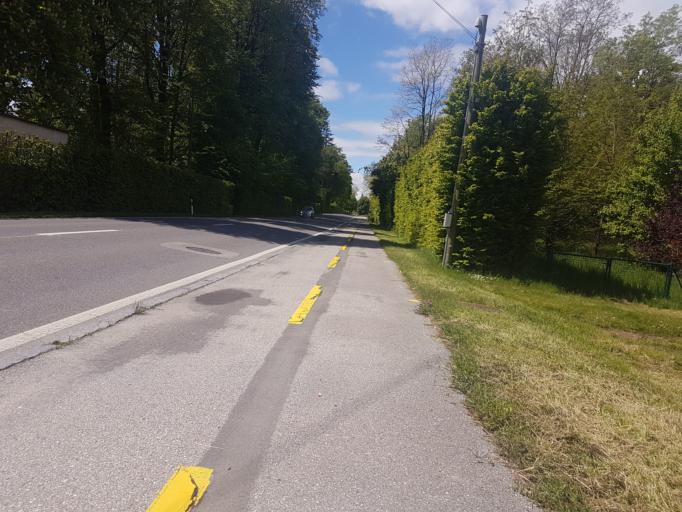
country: CH
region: Vaud
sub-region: Nyon District
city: Rolle
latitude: 46.4468
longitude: 6.3241
